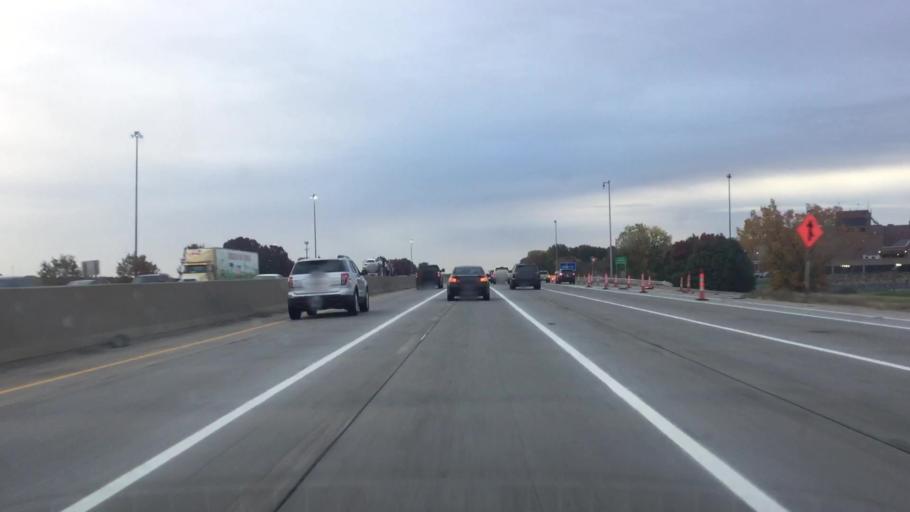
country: US
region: Kansas
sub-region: Johnson County
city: Leawood
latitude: 38.9336
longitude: -94.6245
